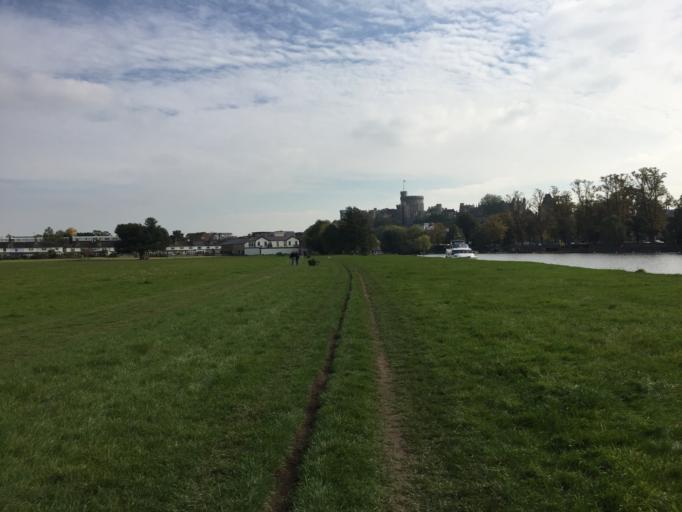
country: GB
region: England
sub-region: West Berkshire
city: Eton
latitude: 51.4860
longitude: -0.6145
